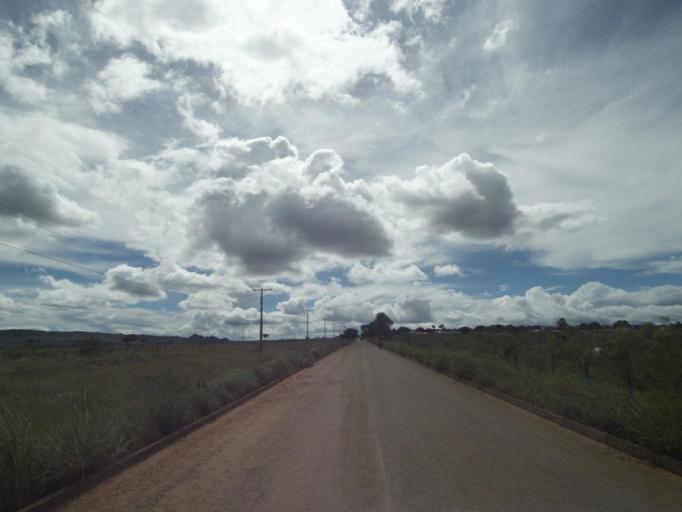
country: BR
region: Goias
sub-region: Pirenopolis
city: Pirenopolis
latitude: -15.7870
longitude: -48.7814
